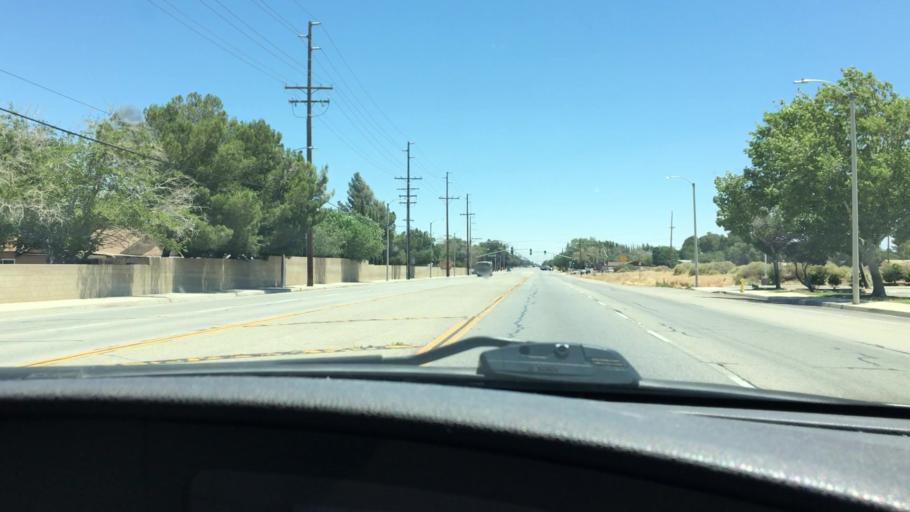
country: US
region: California
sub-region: Los Angeles County
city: Quartz Hill
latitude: 34.6602
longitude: -118.1953
